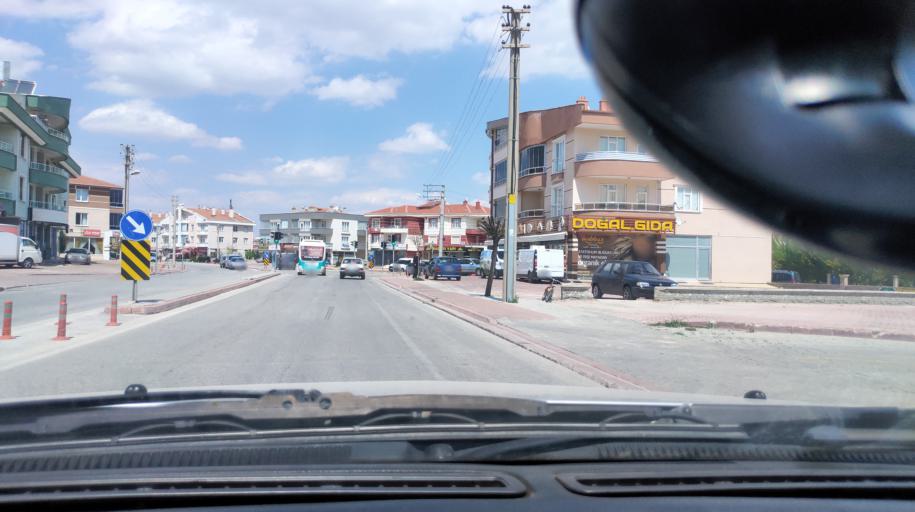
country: TR
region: Konya
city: Selcuklu
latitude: 37.9288
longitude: 32.4874
